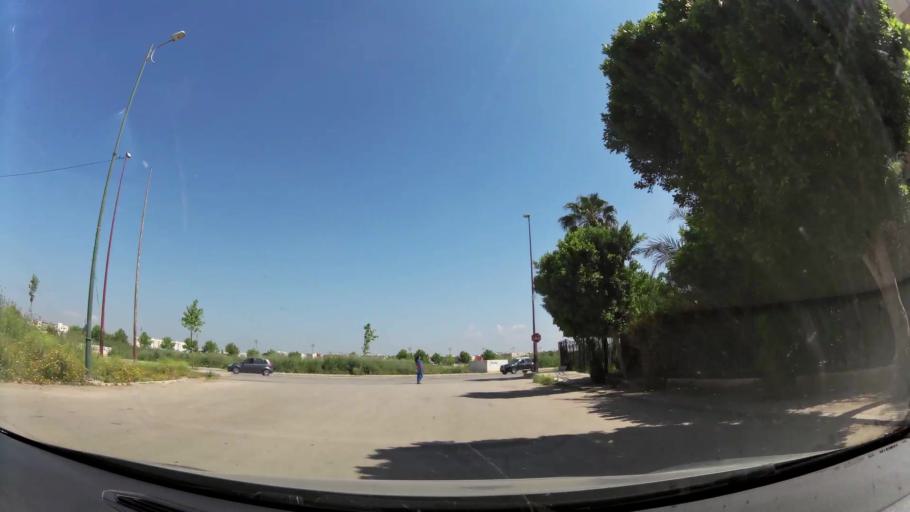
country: MA
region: Fes-Boulemane
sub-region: Fes
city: Fes
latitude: 34.0145
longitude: -5.0214
